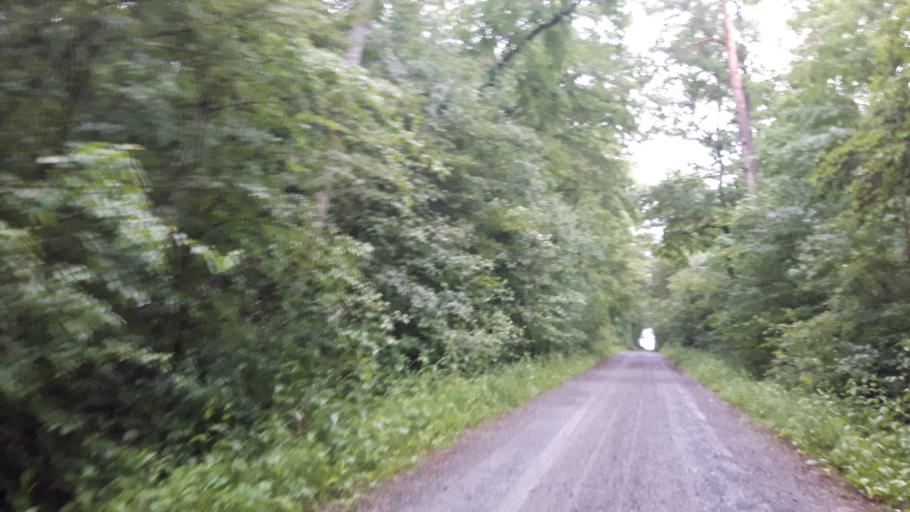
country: DE
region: Bavaria
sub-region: Regierungsbezirk Unterfranken
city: Uchtelhausen
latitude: 50.1242
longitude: 10.2929
